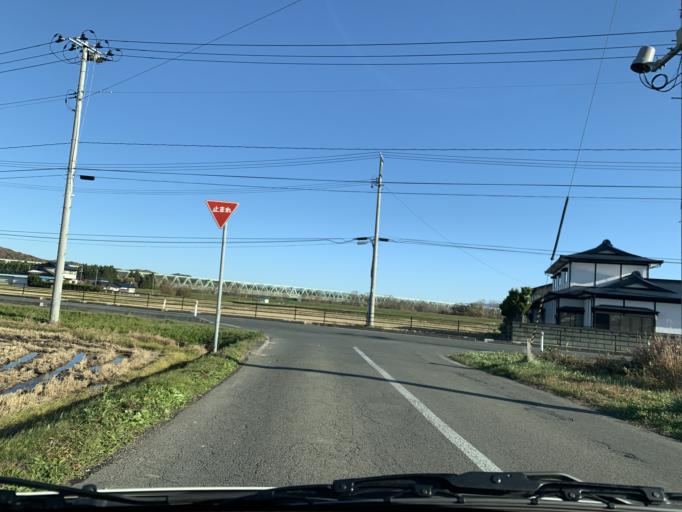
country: JP
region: Iwate
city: Kitakami
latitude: 39.2490
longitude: 141.1049
